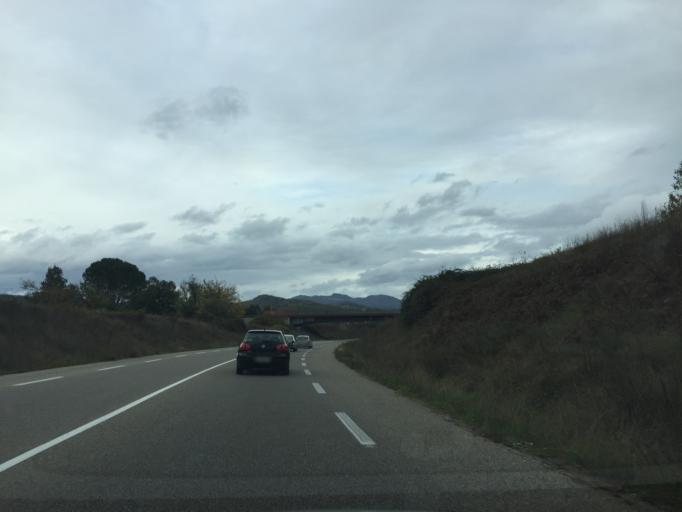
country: FR
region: Rhone-Alpes
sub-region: Departement de l'Ardeche
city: Saint-Privat
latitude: 44.6169
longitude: 4.4091
